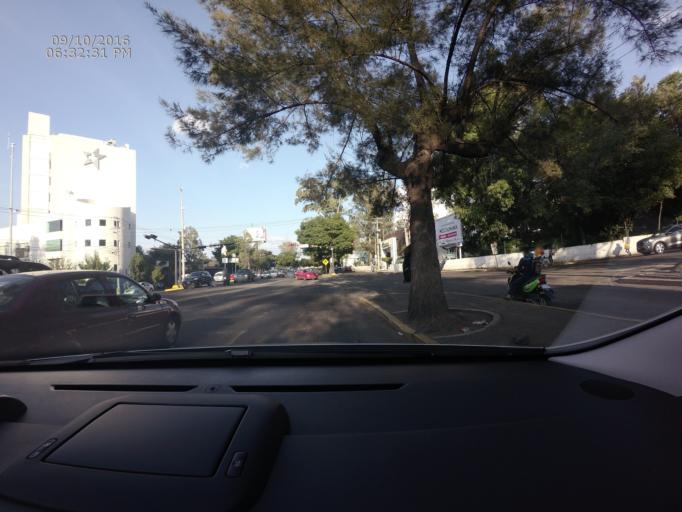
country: MX
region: Michoacan
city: Morelia
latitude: 19.6821
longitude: -101.1923
